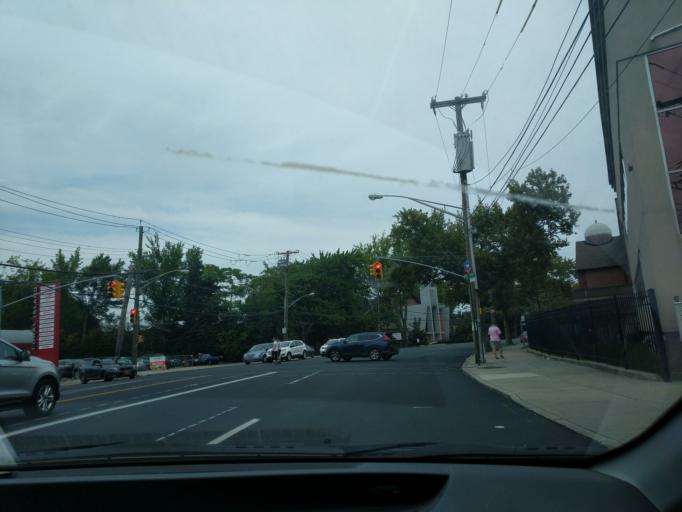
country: US
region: New York
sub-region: Richmond County
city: Bloomfield
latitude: 40.6076
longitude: -74.1624
